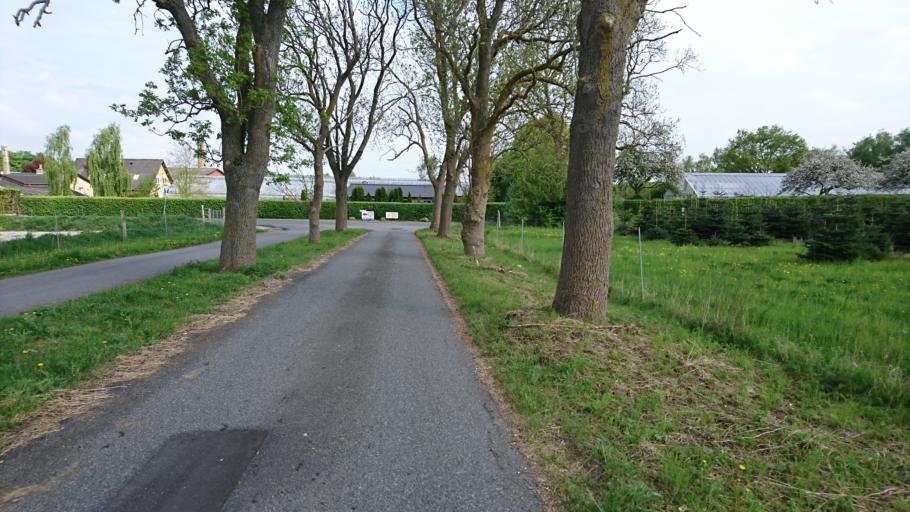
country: DK
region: Capital Region
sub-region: Egedal Kommune
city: Smorumnedre
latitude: 55.7304
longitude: 12.3157
